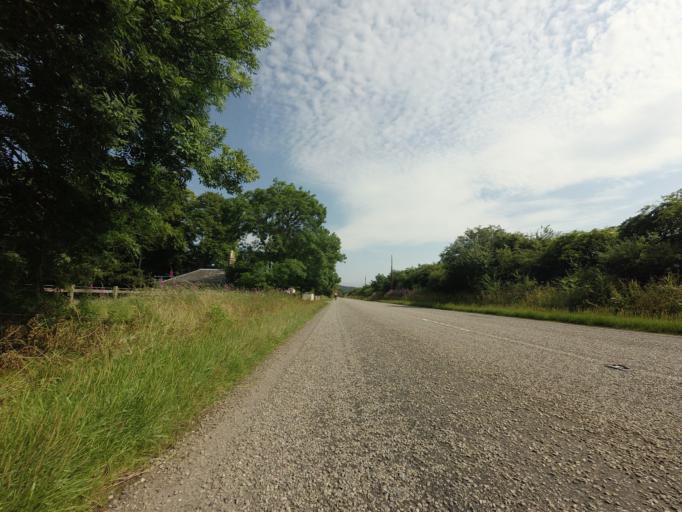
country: GB
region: Scotland
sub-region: Highland
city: Alness
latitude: 57.9139
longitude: -4.3818
